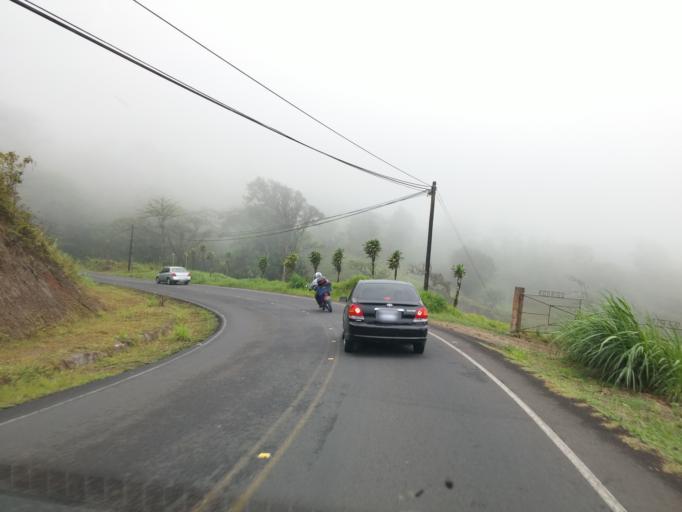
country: CR
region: Alajuela
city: San Ramon
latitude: 10.1695
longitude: -84.4953
